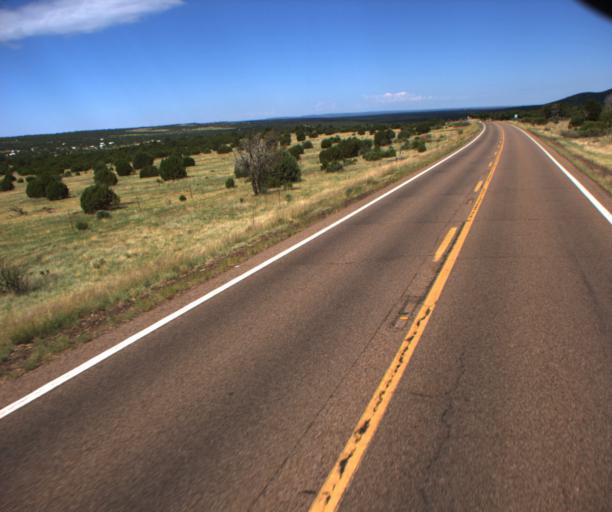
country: US
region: Arizona
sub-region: Navajo County
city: White Mountain Lake
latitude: 34.2851
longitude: -109.8204
